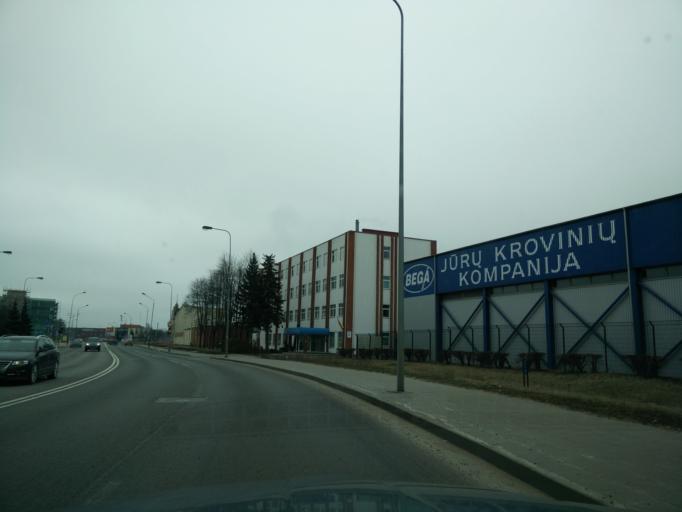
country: LT
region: Klaipedos apskritis
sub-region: Klaipeda
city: Klaipeda
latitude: 55.7001
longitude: 21.1355
